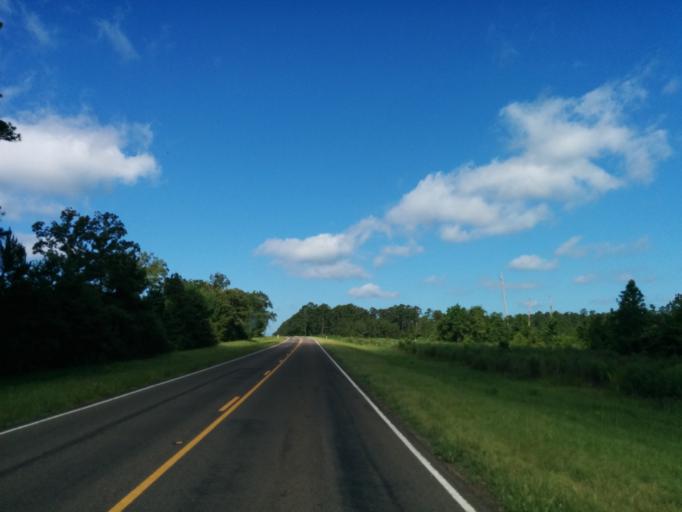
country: US
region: Texas
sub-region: San Augustine County
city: San Augustine
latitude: 31.4101
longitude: -94.0260
